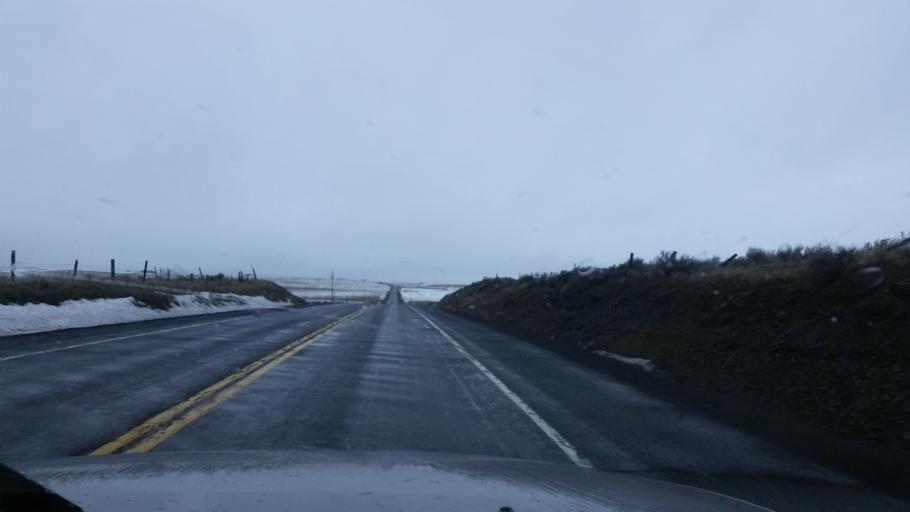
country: US
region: Washington
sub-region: Lincoln County
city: Davenport
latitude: 47.4760
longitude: -118.2742
